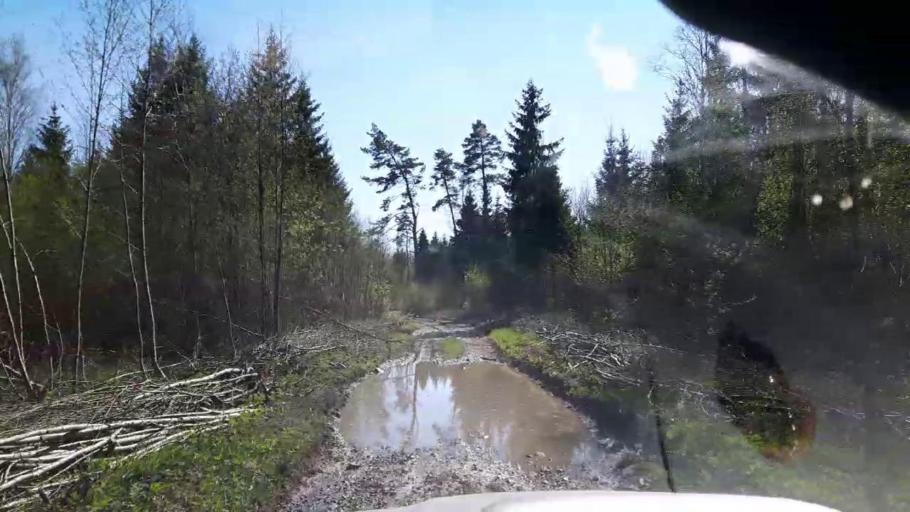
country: EE
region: Paernumaa
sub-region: Tootsi vald
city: Tootsi
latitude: 58.5500
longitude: 24.8001
